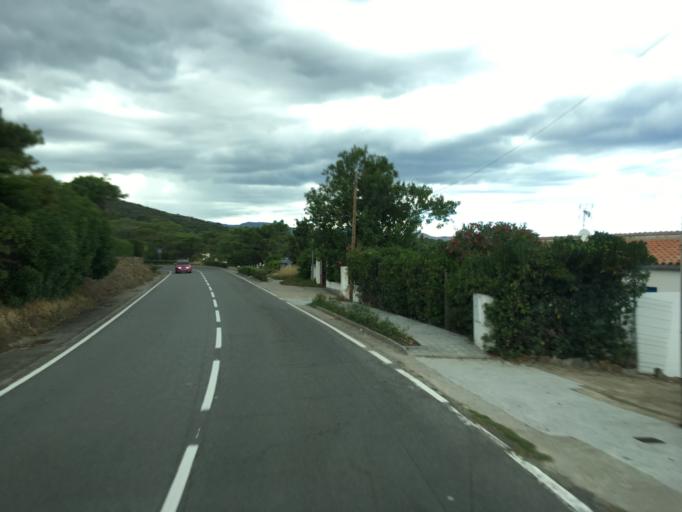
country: ES
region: Catalonia
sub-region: Provincia de Girona
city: Llanca
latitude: 42.3410
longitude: 3.1884
